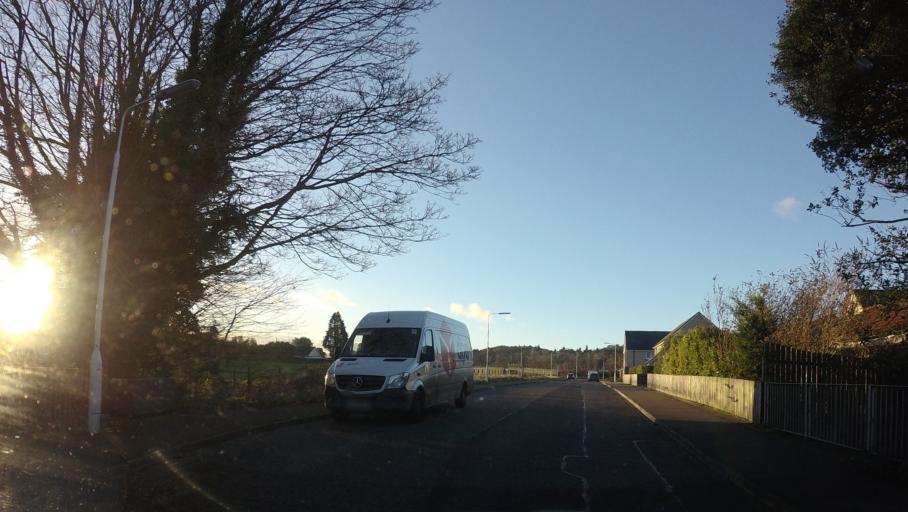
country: GB
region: Scotland
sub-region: Fife
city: Tayport
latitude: 56.4419
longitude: -2.8820
